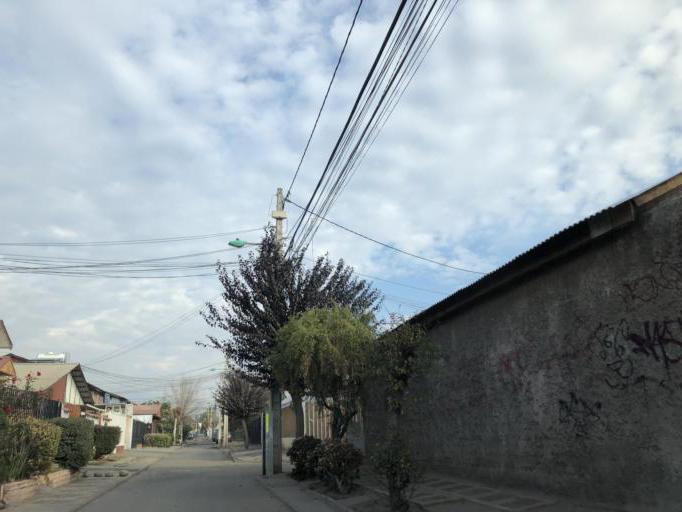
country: CL
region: Santiago Metropolitan
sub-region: Provincia de Cordillera
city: Puente Alto
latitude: -33.5985
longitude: -70.5574
